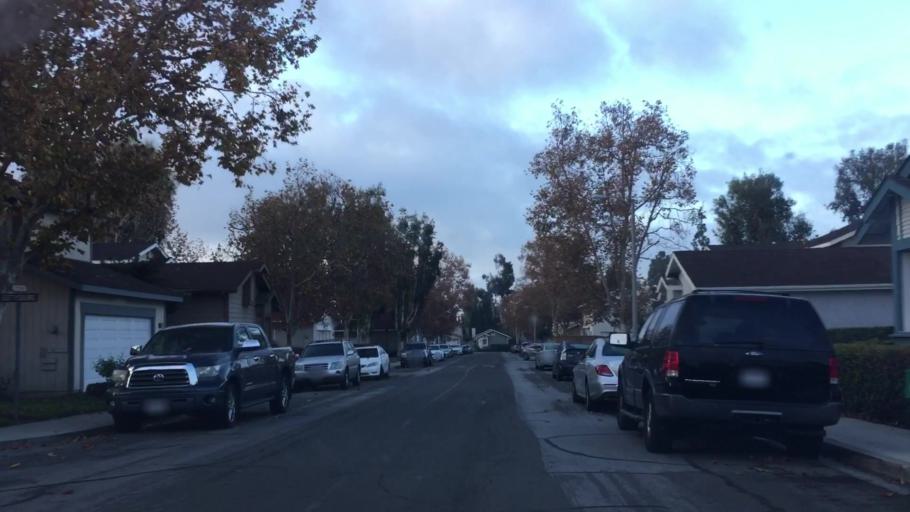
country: US
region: California
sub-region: Orange County
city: North Tustin
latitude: 33.7074
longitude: -117.7733
